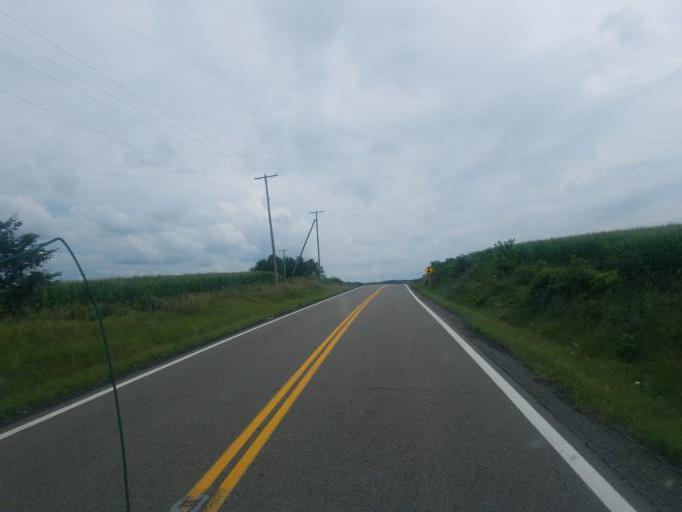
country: US
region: Ohio
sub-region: Knox County
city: Oak Hill
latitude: 40.3405
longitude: -82.1558
